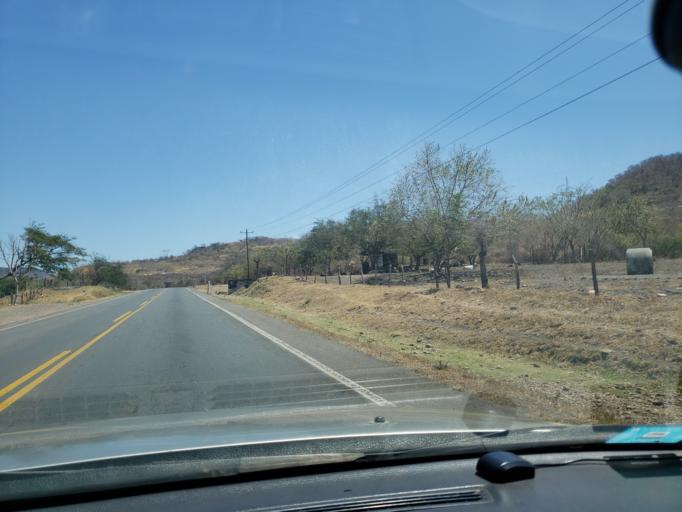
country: NI
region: Boaco
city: Teustepe
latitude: 12.3453
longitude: -85.9348
